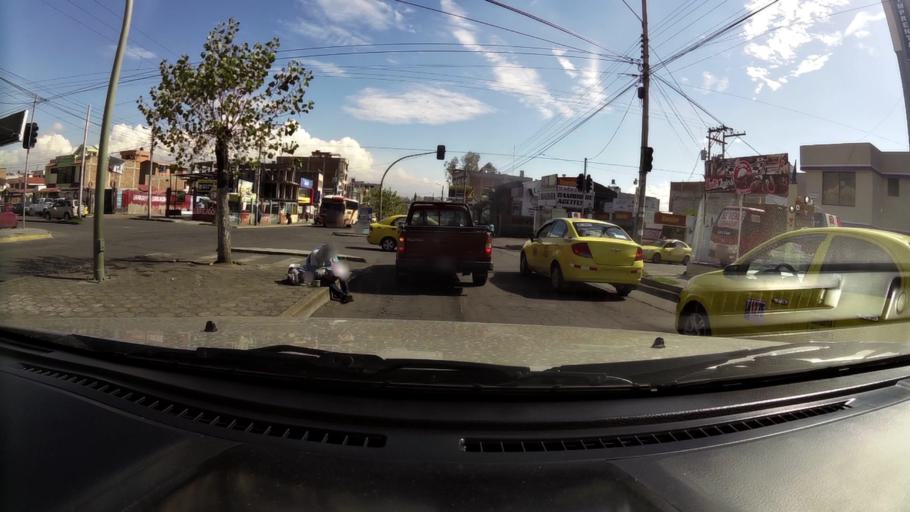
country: EC
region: Chimborazo
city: Riobamba
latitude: -1.6647
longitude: -78.6649
